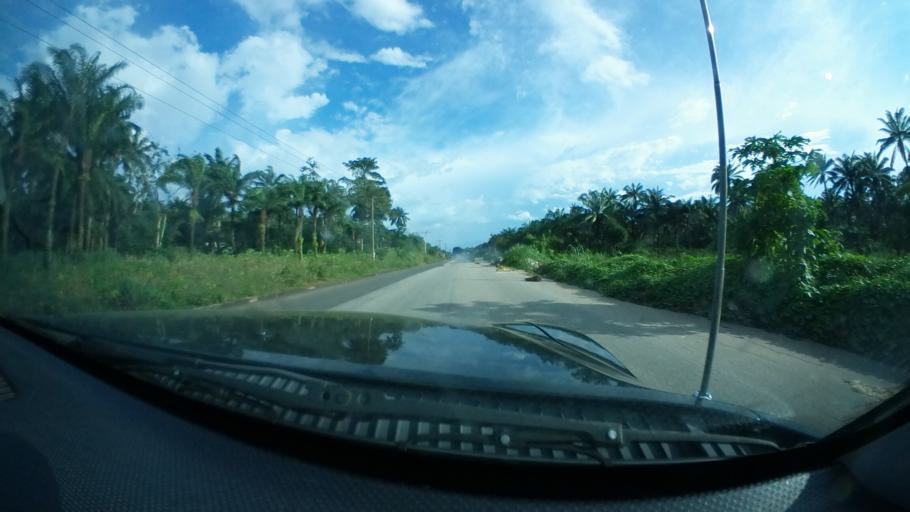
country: NG
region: Imo
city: Orodo
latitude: 5.6834
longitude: 7.0109
